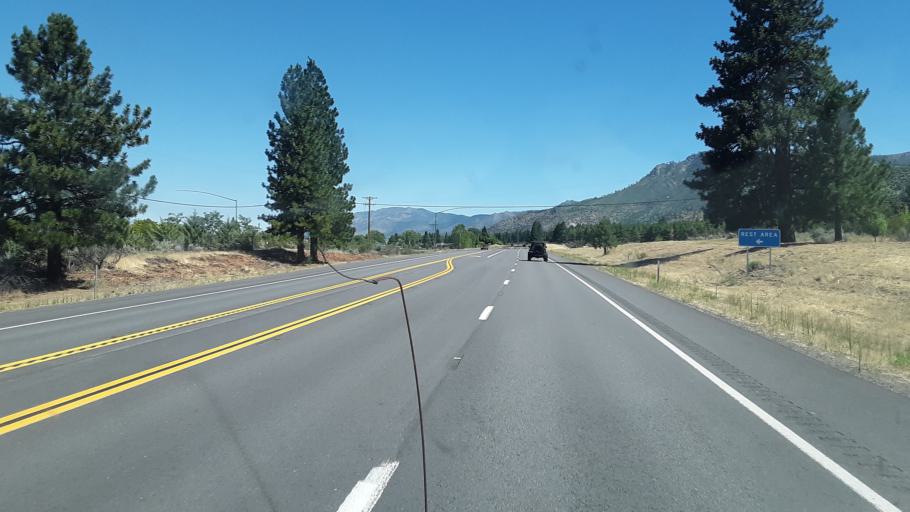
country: US
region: California
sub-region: Lassen County
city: Janesville
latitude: 40.2569
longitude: -120.4669
